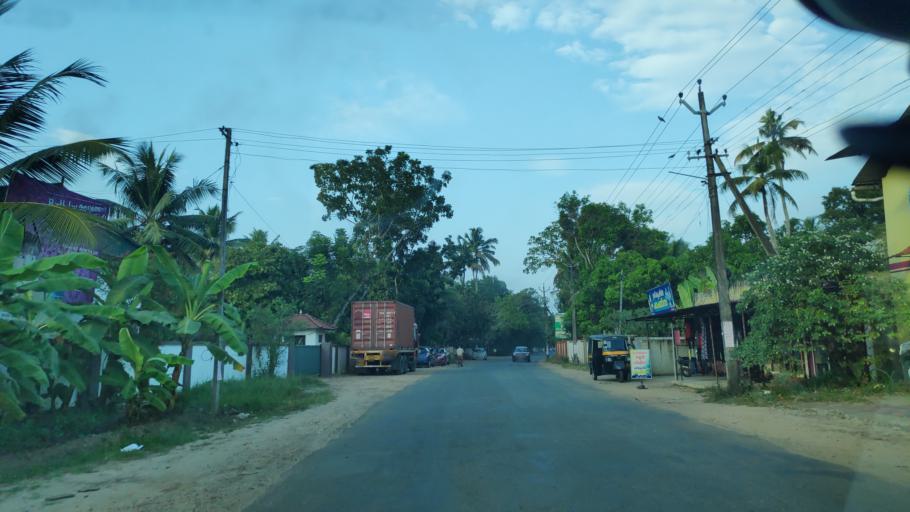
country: IN
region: Kerala
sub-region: Alappuzha
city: Shertallai
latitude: 9.6192
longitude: 76.3640
